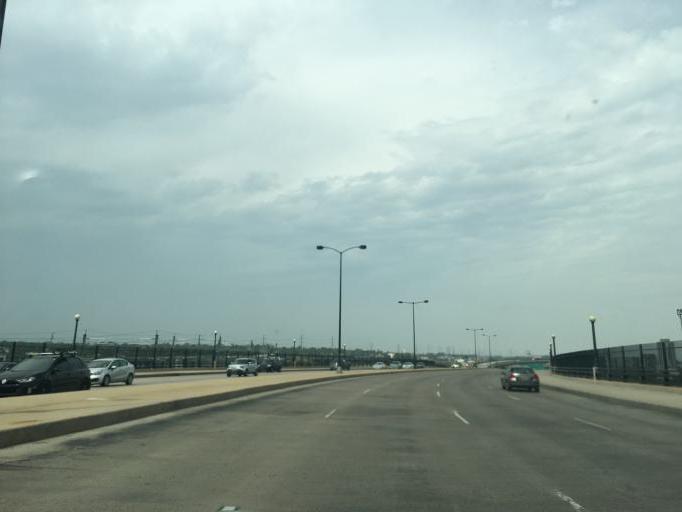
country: US
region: Colorado
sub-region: Denver County
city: Denver
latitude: 39.7603
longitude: -104.9944
